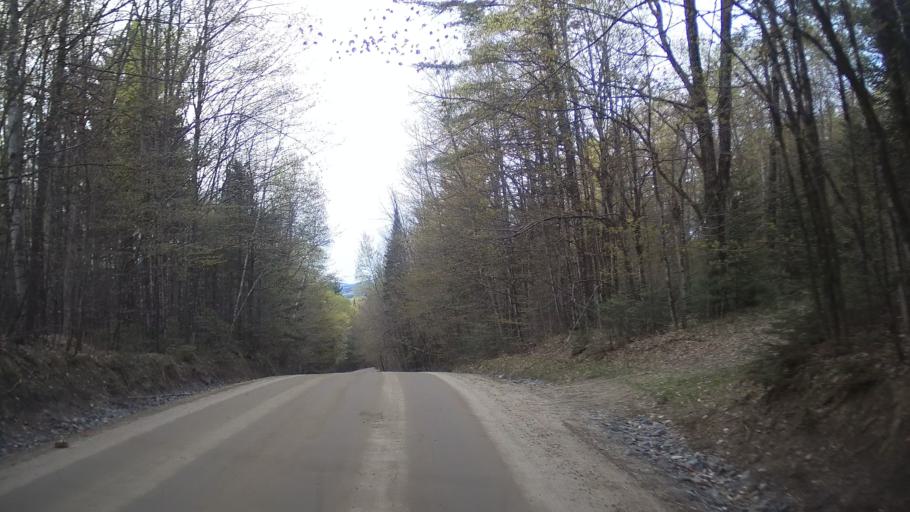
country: US
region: Vermont
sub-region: Caledonia County
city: Lyndonville
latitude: 44.5970
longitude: -71.9595
